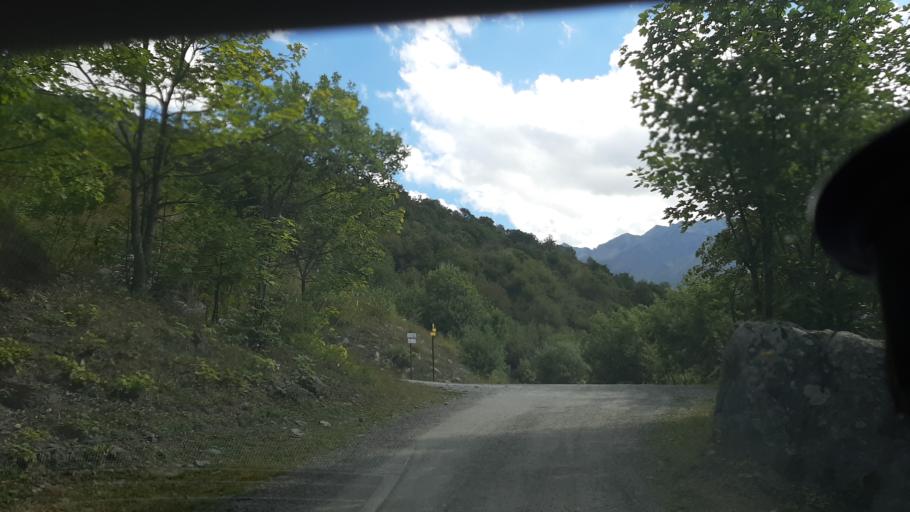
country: FR
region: Rhone-Alpes
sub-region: Departement de la Savoie
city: Saint-Michel-de-Maurienne
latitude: 45.1660
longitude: 6.4939
